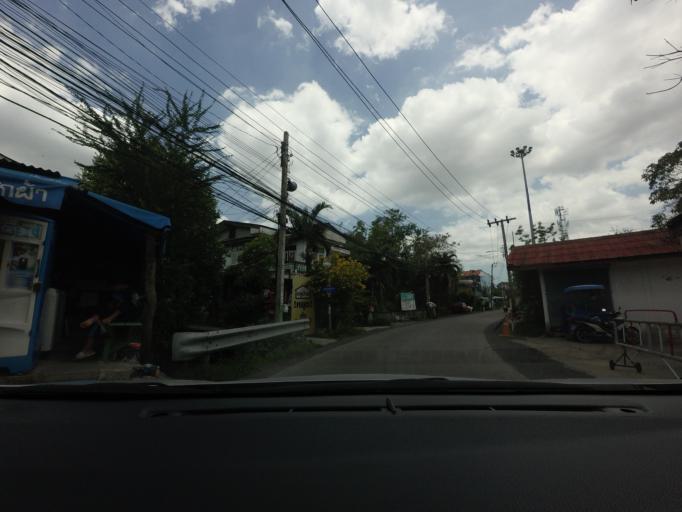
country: TH
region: Samut Prakan
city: Phra Samut Chedi
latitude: 13.6198
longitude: 100.5777
